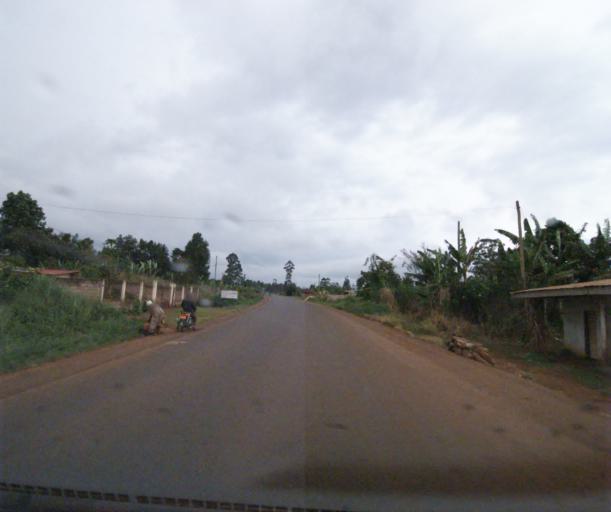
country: CM
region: West
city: Dschang
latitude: 5.4911
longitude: 10.1661
